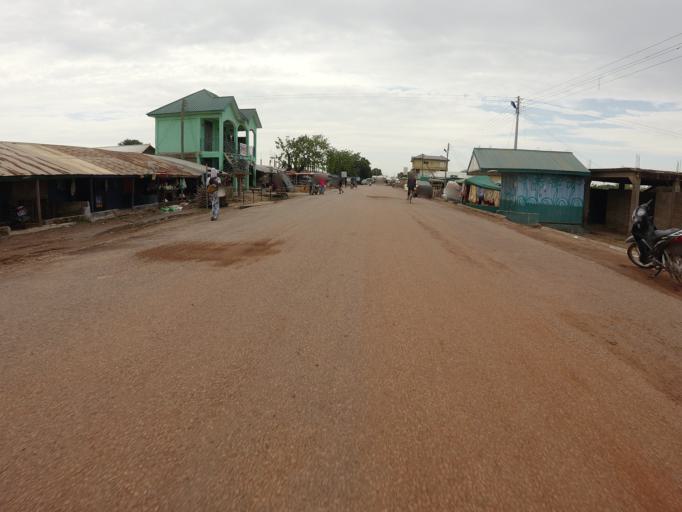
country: GH
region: Upper East
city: Bawku
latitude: 10.9382
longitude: -0.4870
